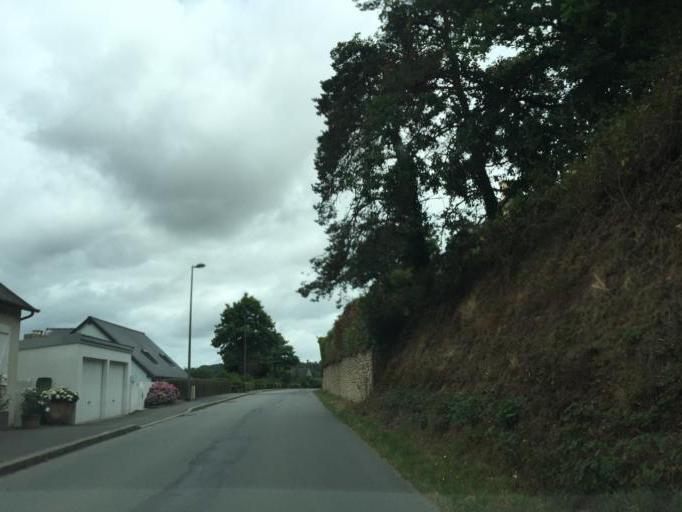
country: FR
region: Brittany
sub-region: Departement des Cotes-d'Armor
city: Jugon-les-Lacs
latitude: 48.4048
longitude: -2.3210
